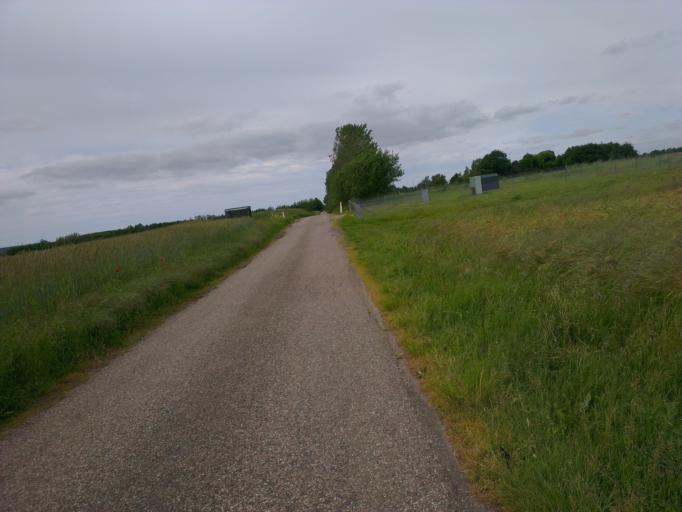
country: DK
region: Capital Region
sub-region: Frederikssund Kommune
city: Frederikssund
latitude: 55.8117
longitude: 12.0785
